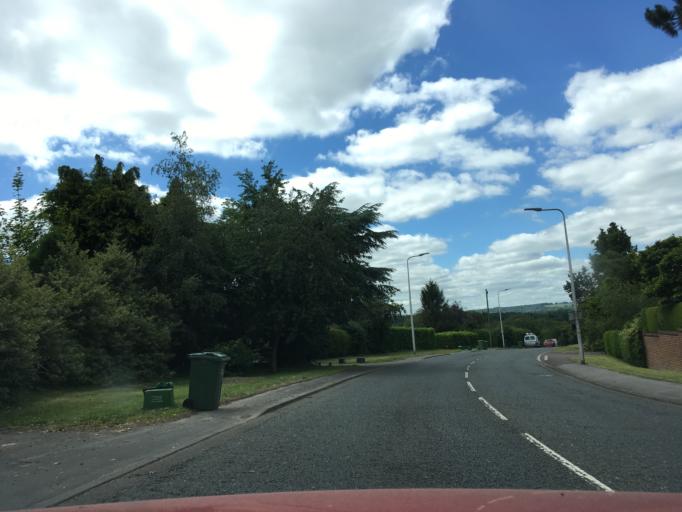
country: GB
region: England
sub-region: West Berkshire
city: Newbury
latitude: 51.3712
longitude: -1.3471
